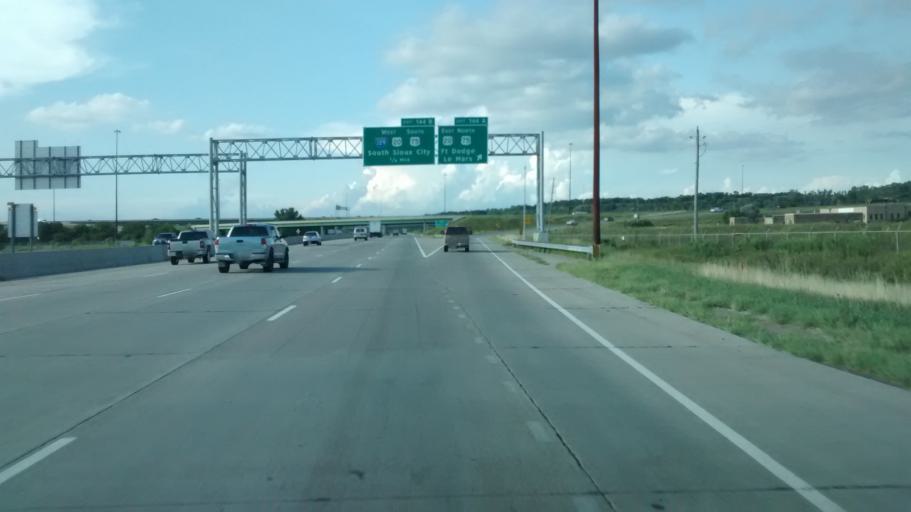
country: US
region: Iowa
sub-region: Woodbury County
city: Sergeant Bluff
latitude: 42.4406
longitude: -96.3752
